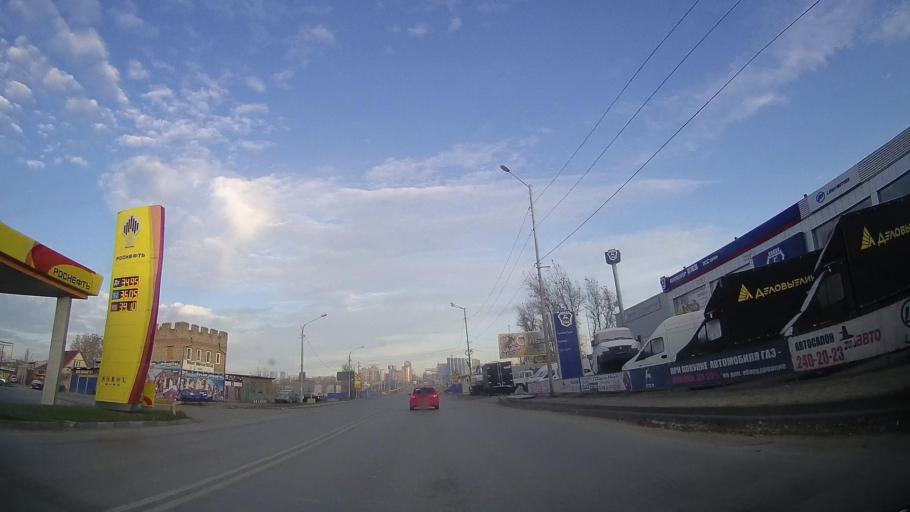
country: RU
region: Rostov
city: Rostov-na-Donu
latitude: 47.2054
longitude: 39.7265
